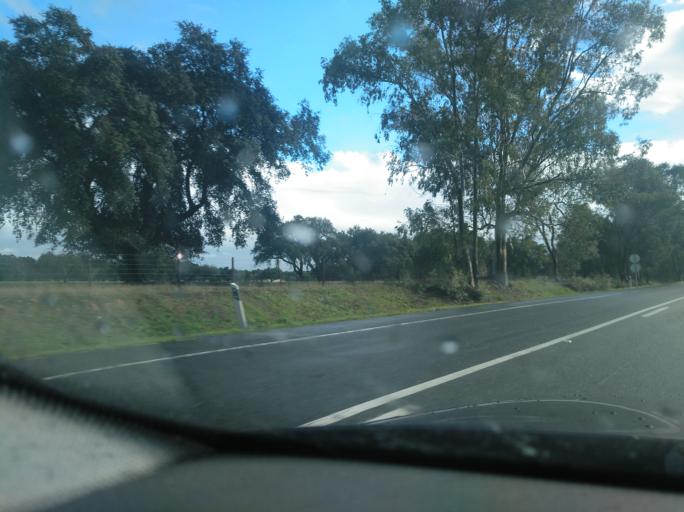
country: PT
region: Setubal
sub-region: Grandola
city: Grandola
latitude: 38.0330
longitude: -8.4003
